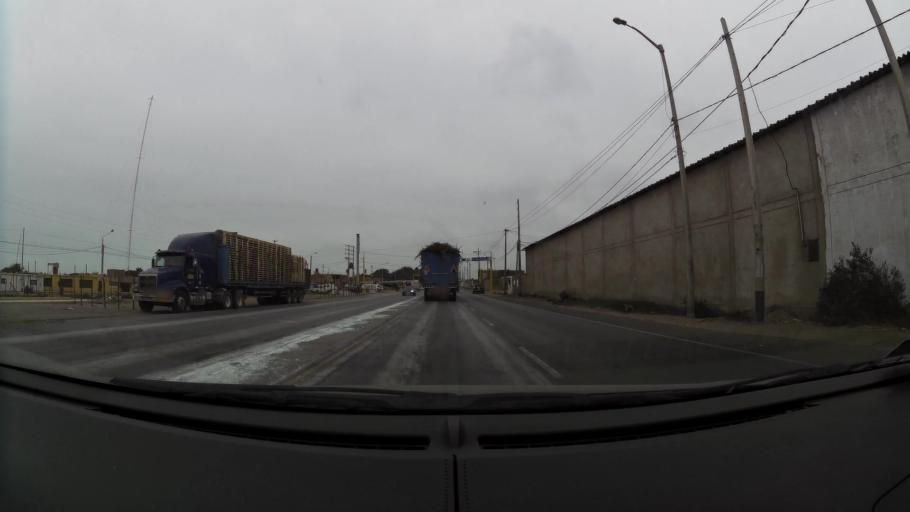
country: PE
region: La Libertad
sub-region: Provincia de Trujillo
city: Moche
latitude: -8.1641
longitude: -79.0099
